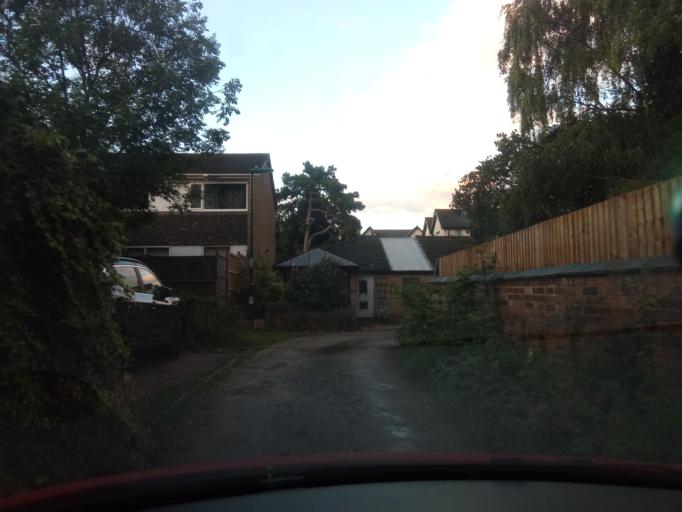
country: GB
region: England
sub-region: Nottingham
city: Nottingham
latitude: 52.9740
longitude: -1.1372
